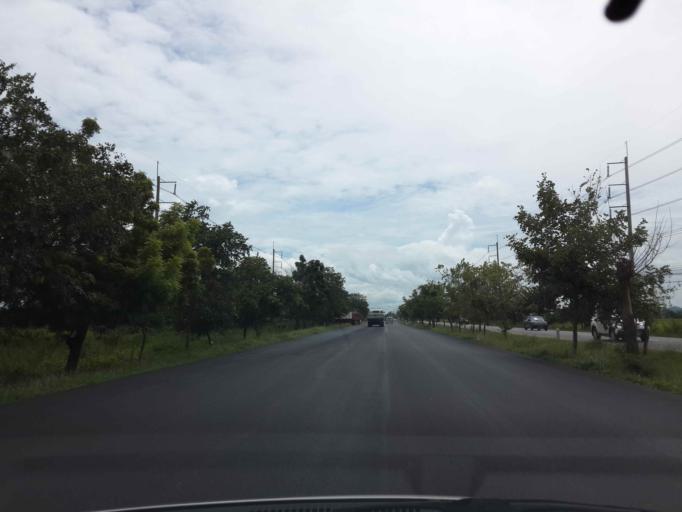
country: TH
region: Ratchaburi
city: Pak Tho
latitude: 13.4234
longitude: 99.8084
